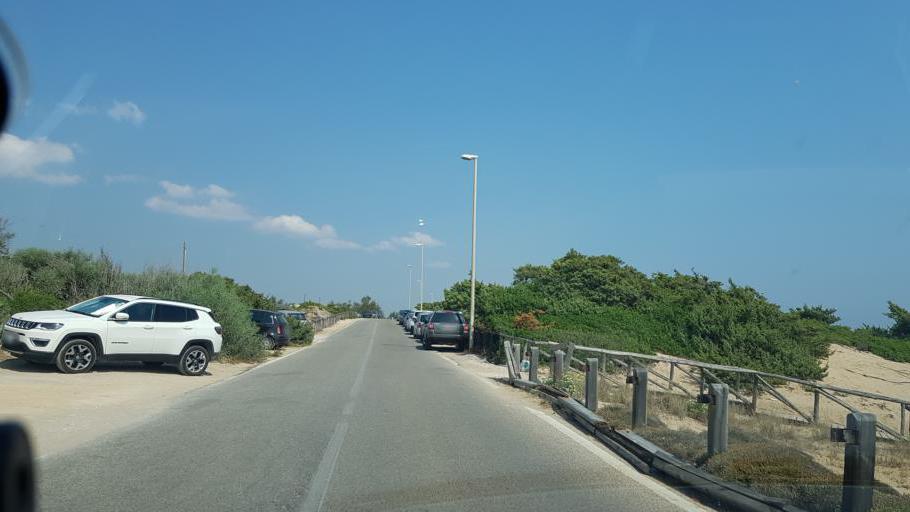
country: IT
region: Apulia
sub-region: Provincia di Taranto
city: Maruggio
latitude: 40.3007
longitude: 17.6039
